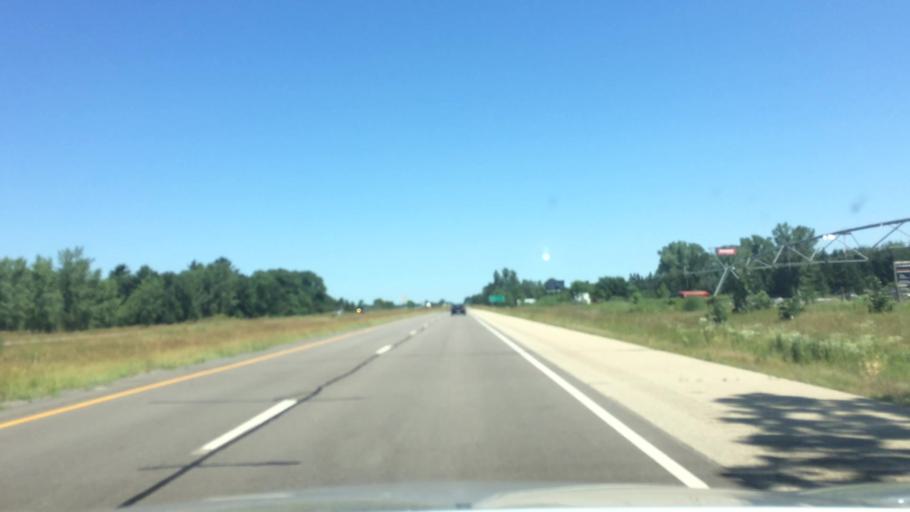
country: US
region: Wisconsin
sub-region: Portage County
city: Plover
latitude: 44.2246
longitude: -89.5243
